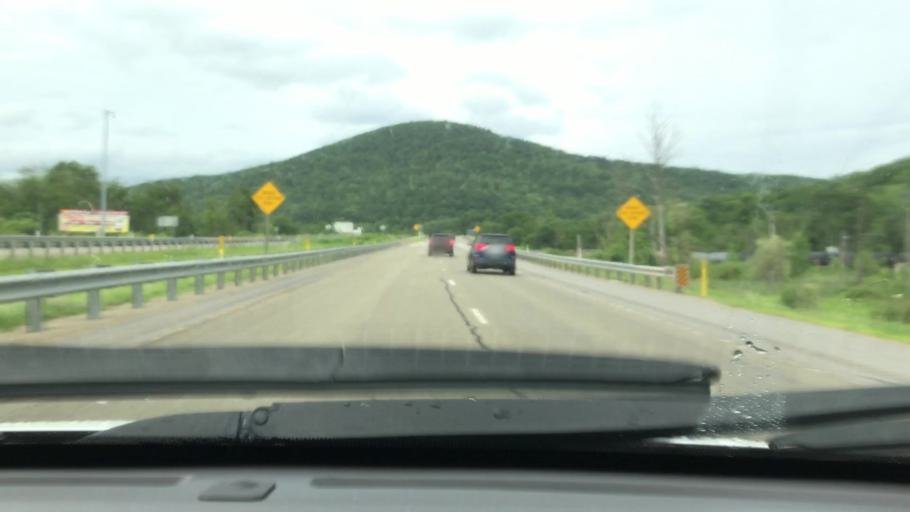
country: US
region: Pennsylvania
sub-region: McKean County
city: Foster Brook
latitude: 41.9952
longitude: -78.6204
